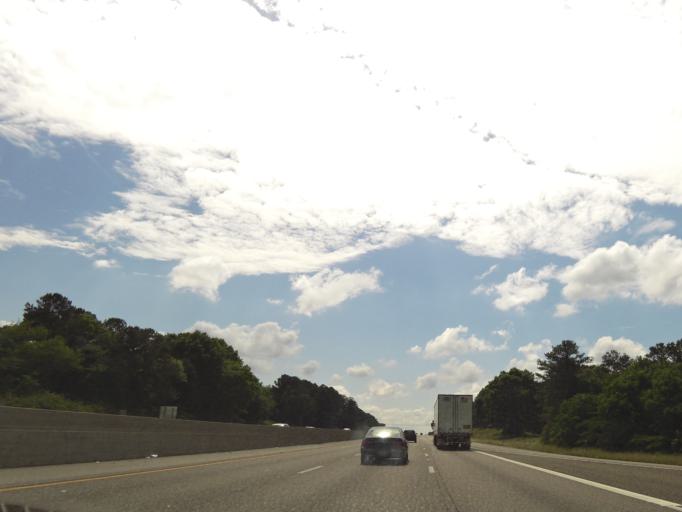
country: US
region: Alabama
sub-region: Calhoun County
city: Bynum
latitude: 33.5839
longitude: -85.9271
